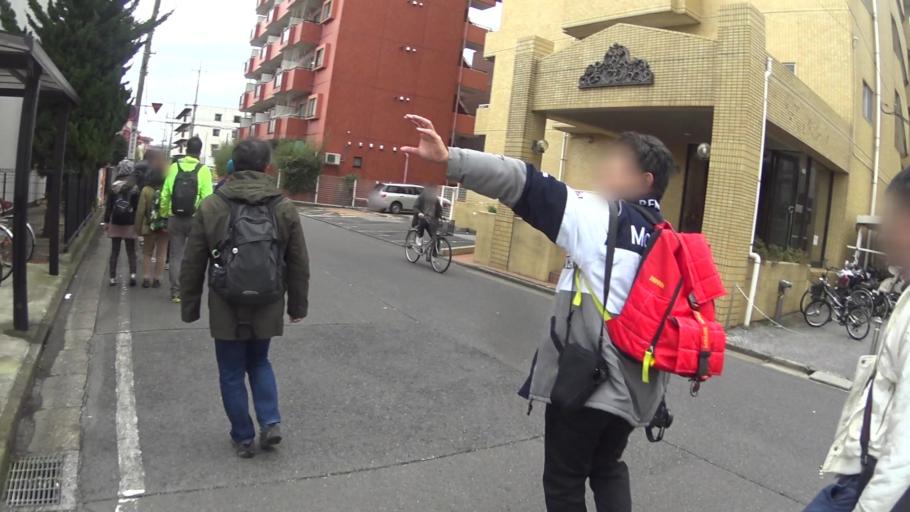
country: JP
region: Chiba
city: Nagareyama
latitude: 35.8425
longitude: 139.8852
